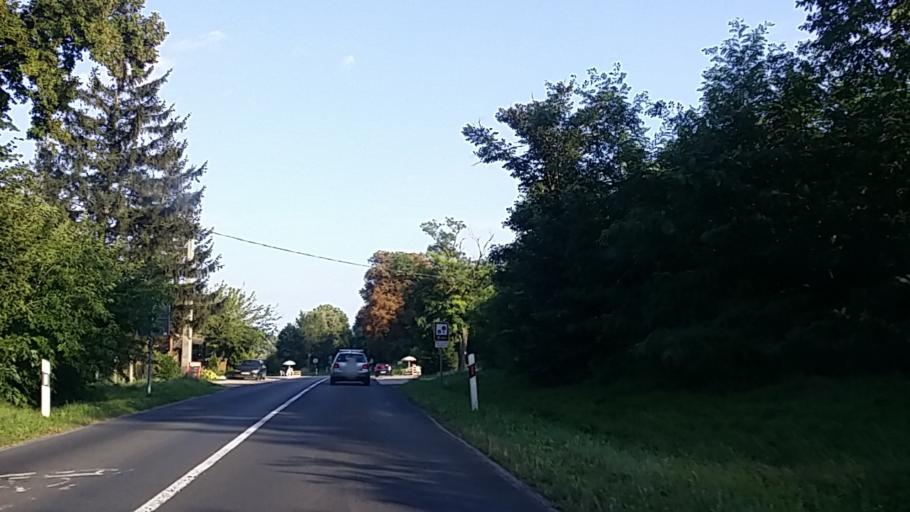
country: HU
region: Zala
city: Keszthely
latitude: 46.7100
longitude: 17.2477
